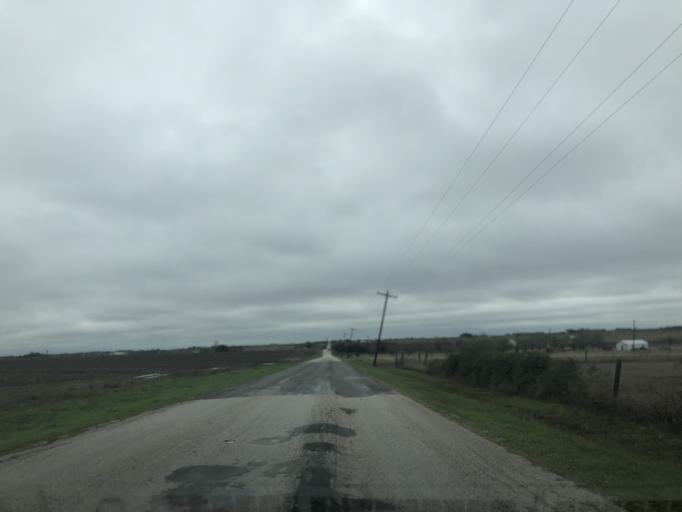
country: US
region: Texas
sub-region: Williamson County
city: Hutto
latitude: 30.5961
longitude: -97.5027
